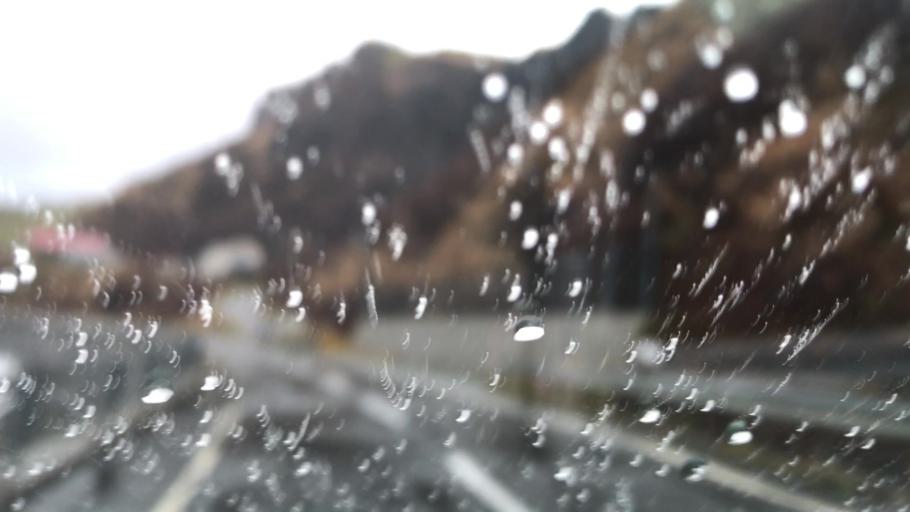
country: JP
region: Hokkaido
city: Iwanai
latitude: 43.3011
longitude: 140.3550
